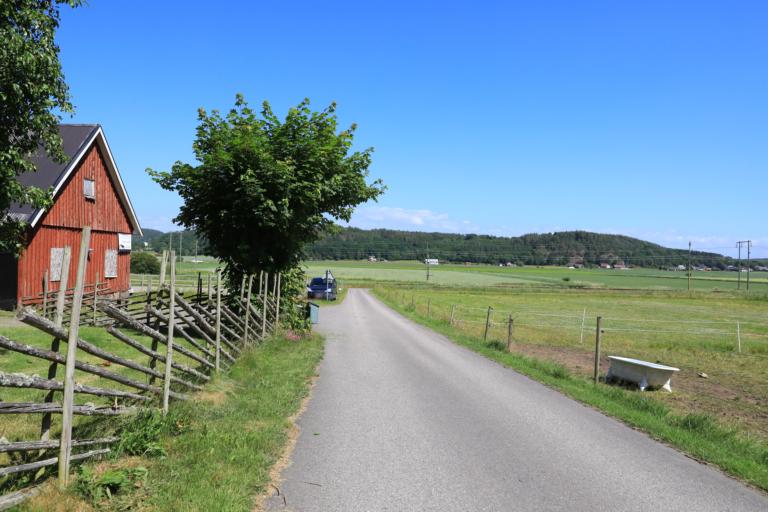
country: SE
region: Halland
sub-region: Varbergs Kommun
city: Veddige
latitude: 57.1788
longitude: 12.3019
